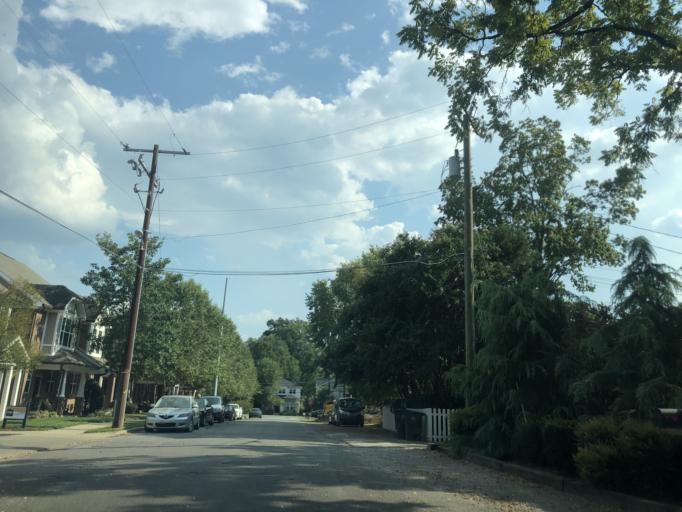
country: US
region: Tennessee
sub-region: Davidson County
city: Nashville
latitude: 36.1271
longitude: -86.7815
